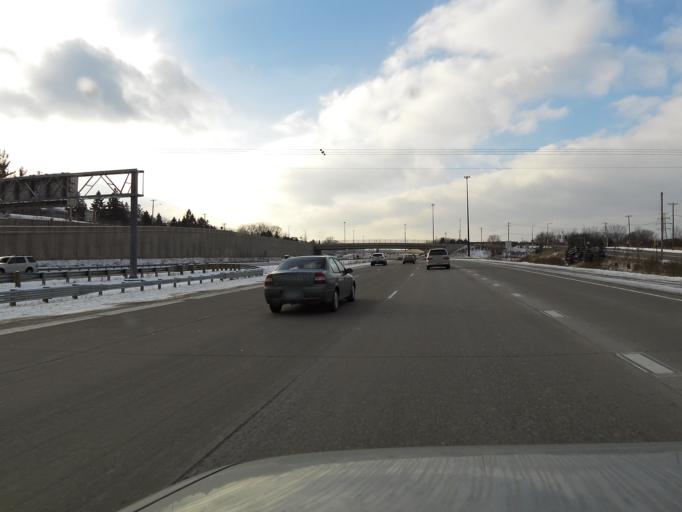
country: US
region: Minnesota
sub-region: Hennepin County
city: Edina
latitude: 44.8605
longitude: -93.3792
